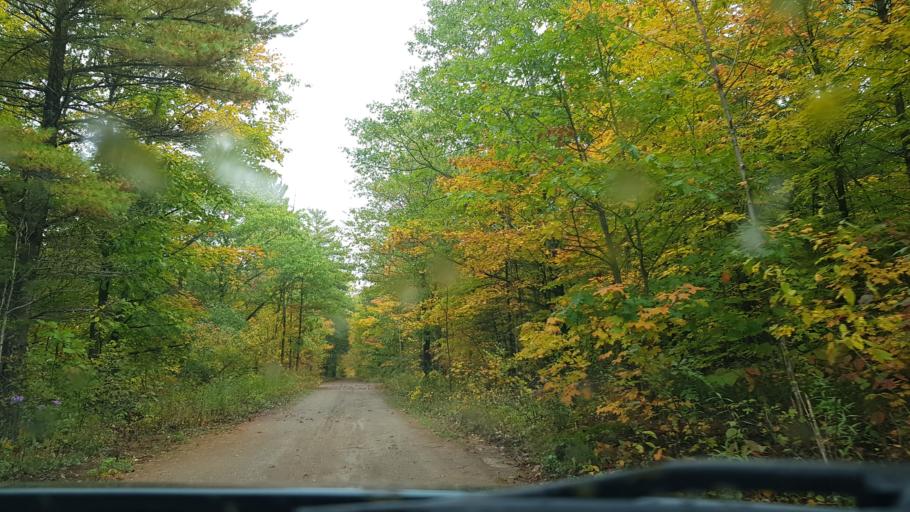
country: CA
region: Ontario
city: Gravenhurst
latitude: 44.6986
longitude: -78.9958
